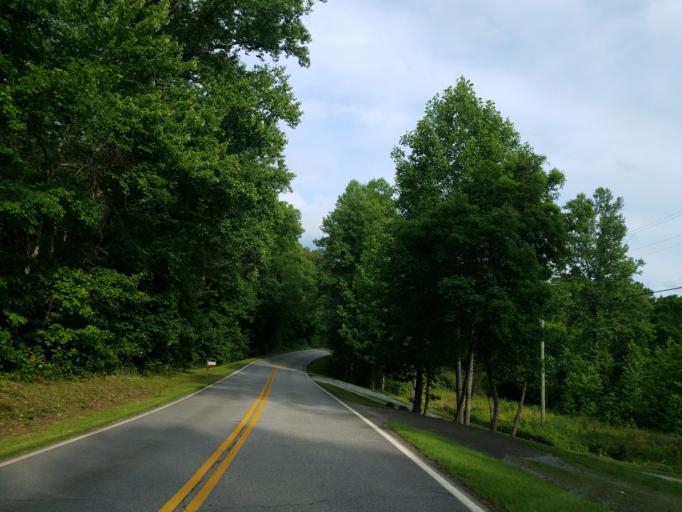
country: US
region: Georgia
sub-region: Lumpkin County
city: Dahlonega
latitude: 34.6110
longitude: -84.0679
